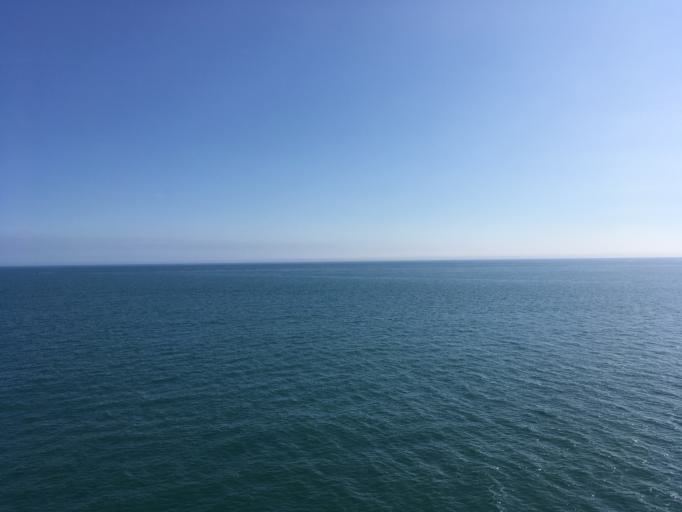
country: IE
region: Leinster
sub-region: Loch Garman
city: Ballygerry
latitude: 52.2501
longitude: -6.2878
